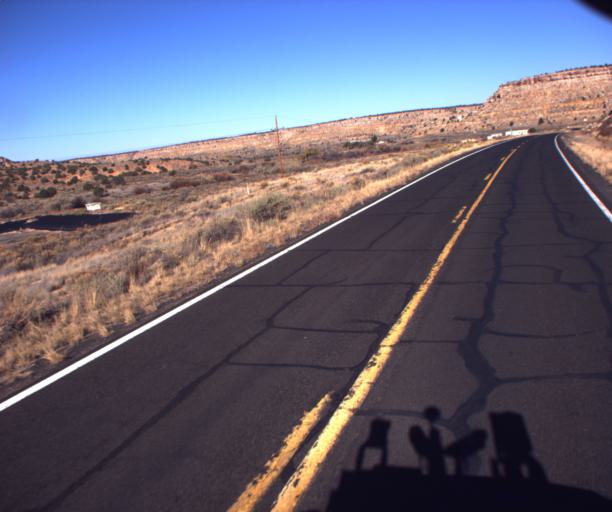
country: US
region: Arizona
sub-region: Navajo County
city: First Mesa
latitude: 35.8332
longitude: -110.2275
